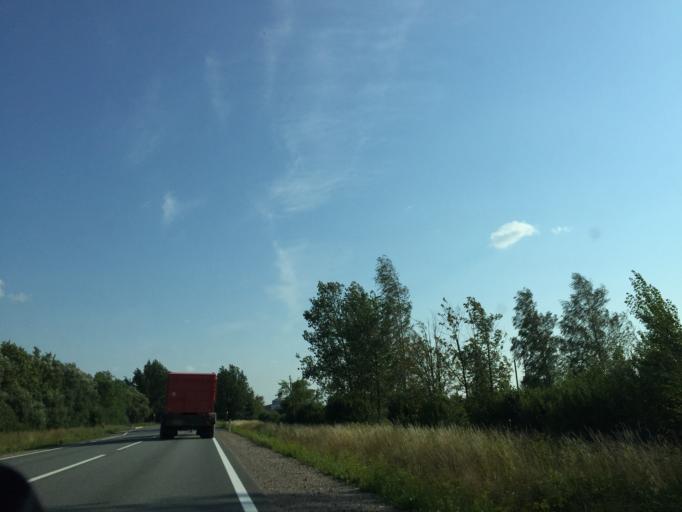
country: LT
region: Siauliu apskritis
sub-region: Joniskis
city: Joniskis
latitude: 56.4276
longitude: 23.6857
